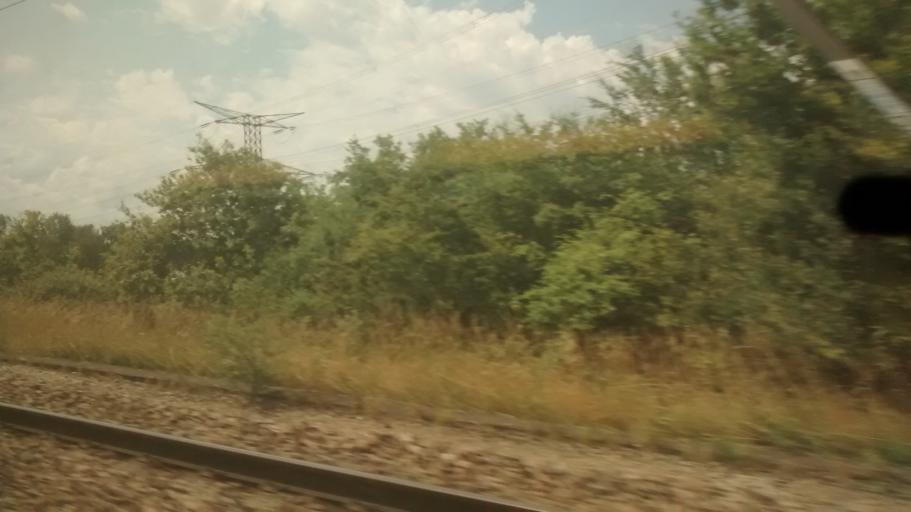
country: FR
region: Bourgogne
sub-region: Departement de Saone-et-Loire
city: Saint-Leu
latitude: 46.7583
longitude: 4.5014
